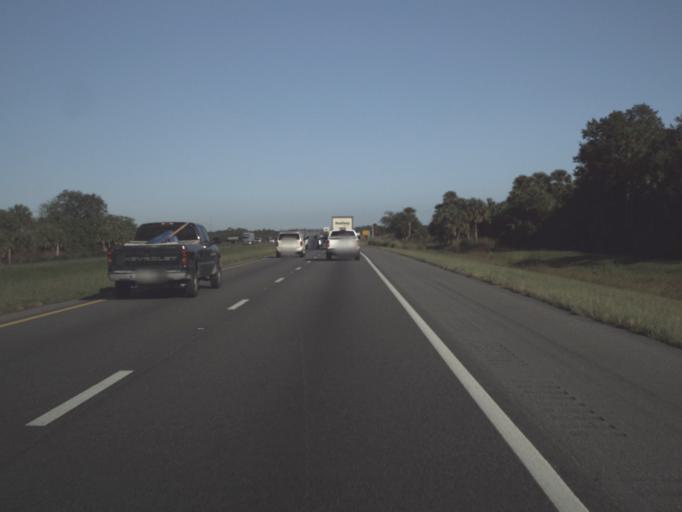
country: US
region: Florida
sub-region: Seminole County
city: Oviedo
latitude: 28.7244
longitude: -81.2458
